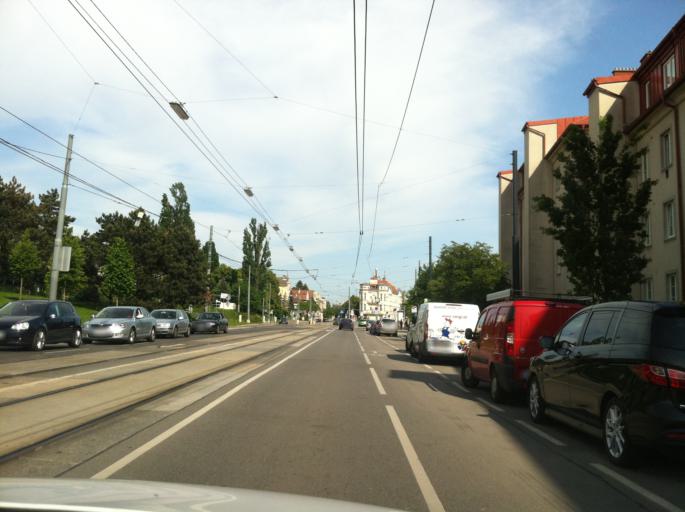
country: AT
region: Lower Austria
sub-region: Politischer Bezirk Modling
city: Perchtoldsdorf
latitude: 48.1995
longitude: 16.2693
